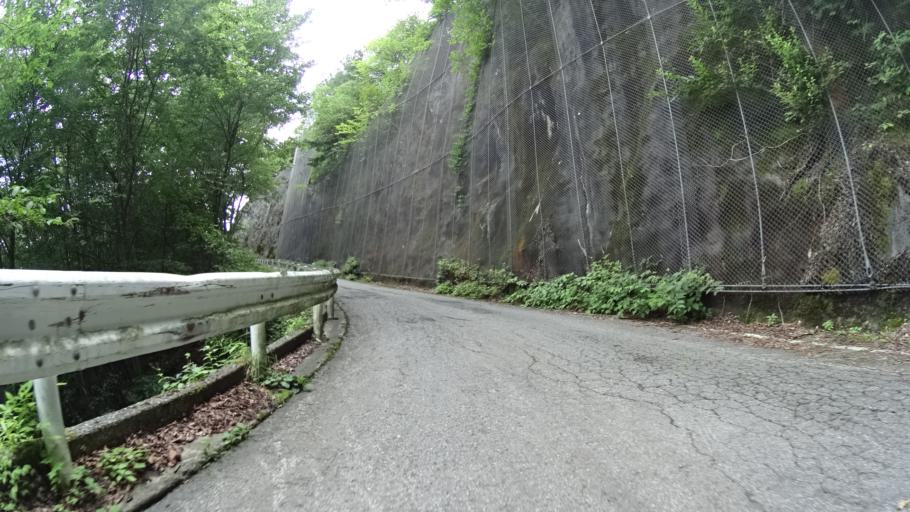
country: JP
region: Nagano
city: Saku
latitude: 36.0709
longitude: 138.6462
